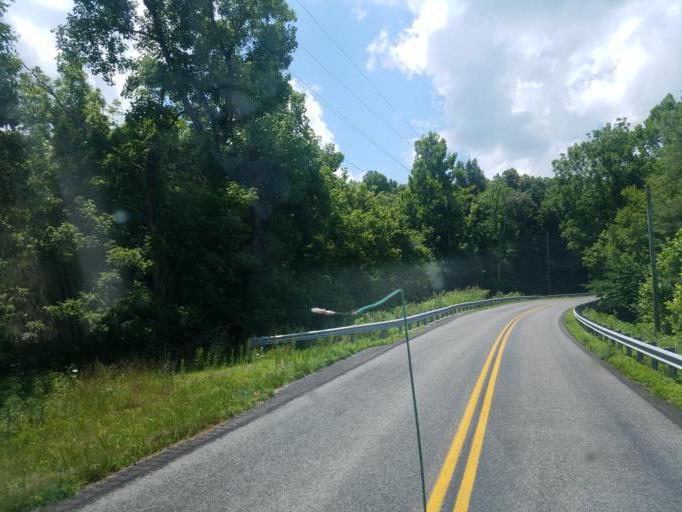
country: US
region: Kentucky
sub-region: Grayson County
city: Leitchfield
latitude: 37.5039
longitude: -86.4722
